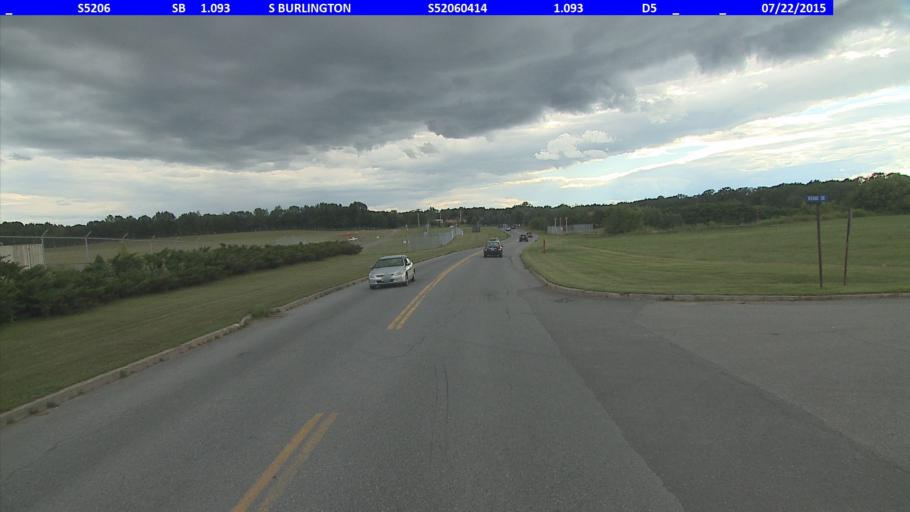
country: US
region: Vermont
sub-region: Chittenden County
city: South Burlington
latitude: 44.4836
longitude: -73.1675
